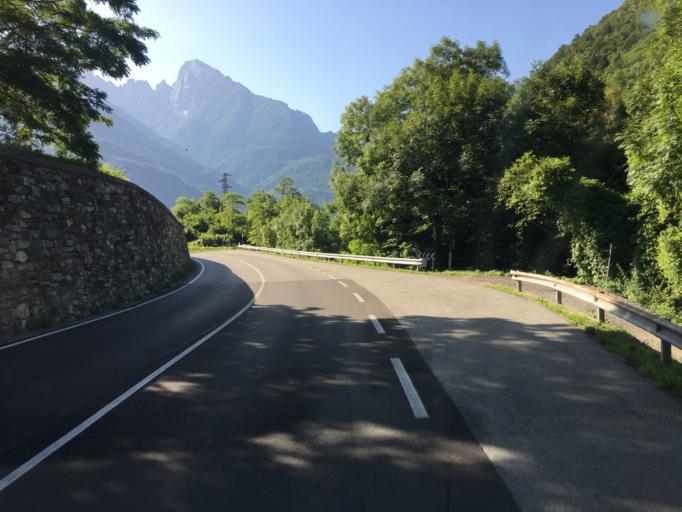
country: IT
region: Lombardy
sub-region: Provincia di Sondrio
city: San Giacomo Filippo
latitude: 46.3256
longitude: 9.3777
